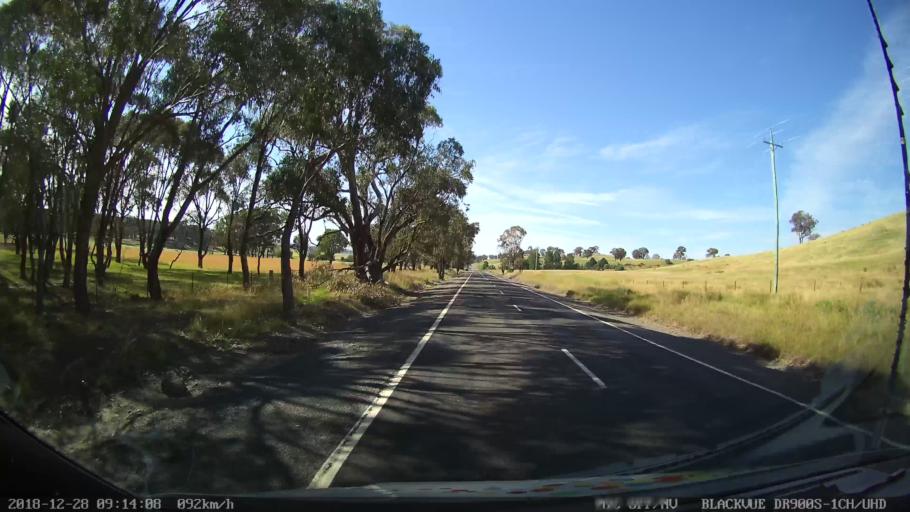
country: AU
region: New South Wales
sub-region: Upper Lachlan Shire
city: Crookwell
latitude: -34.2781
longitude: 149.3453
